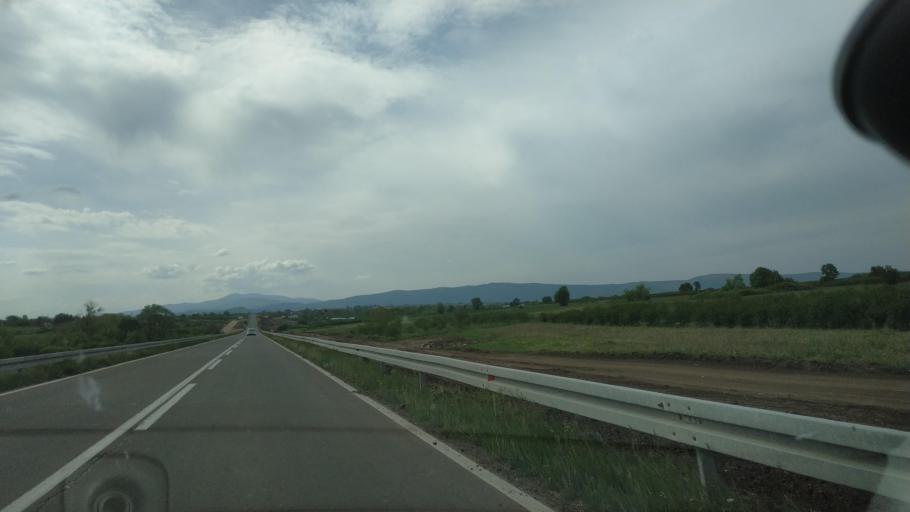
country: RS
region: Central Serbia
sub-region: Nisavski Okrug
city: Merosina
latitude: 43.2823
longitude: 21.7739
